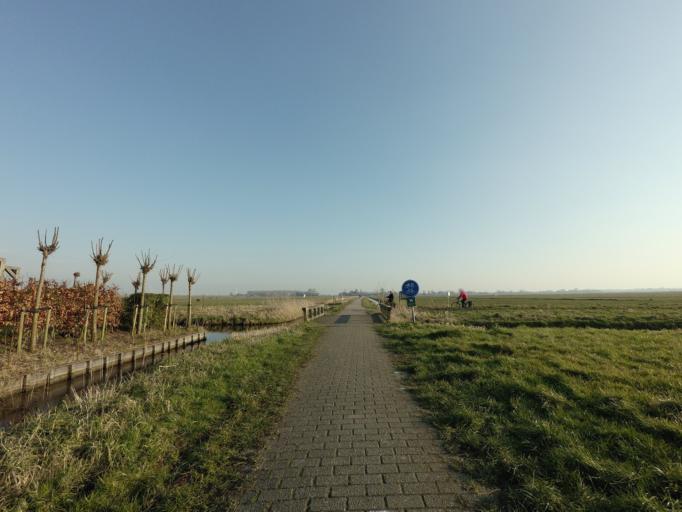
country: NL
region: North Holland
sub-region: Gemeente Haarlem
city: Haarlem
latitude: 52.4098
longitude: 4.6831
